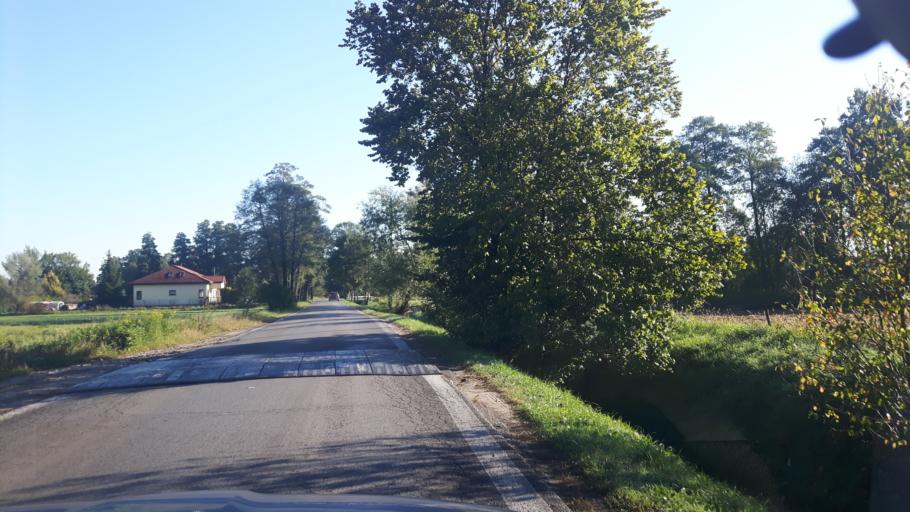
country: PL
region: Masovian Voivodeship
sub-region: Powiat legionowski
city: Stanislawow Pierwszy
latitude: 52.3506
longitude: 21.0147
